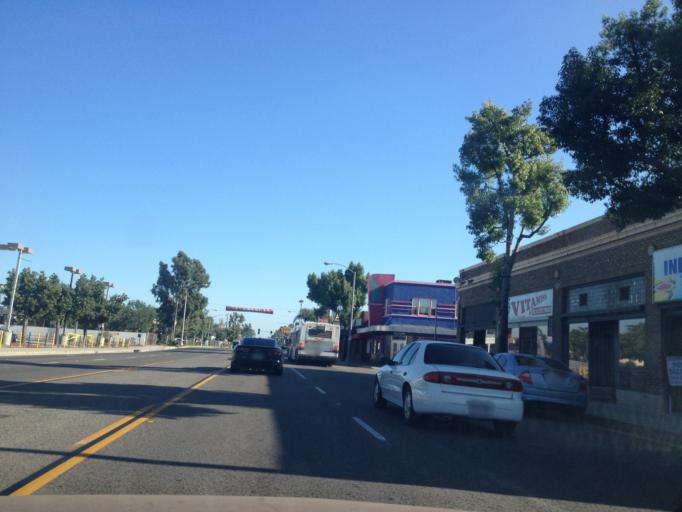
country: US
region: California
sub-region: Orange County
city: Fullerton
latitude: 33.8640
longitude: -117.9243
